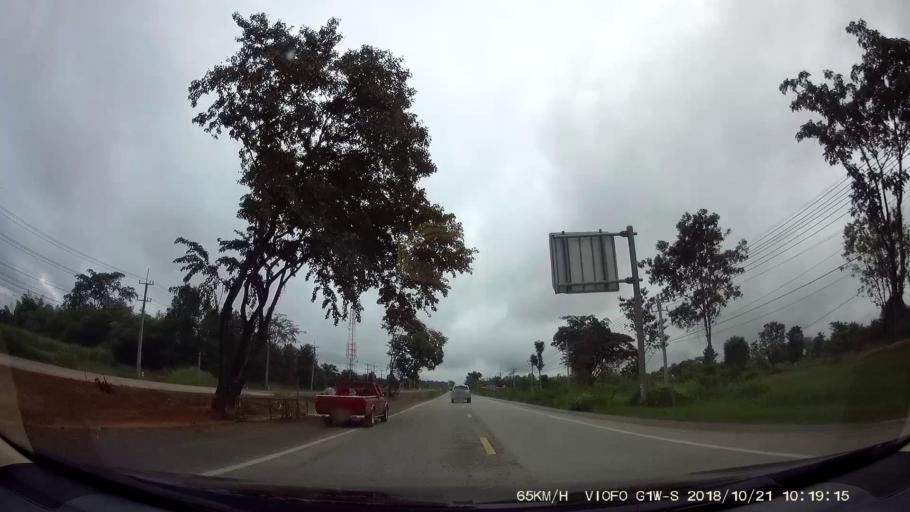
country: TH
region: Chaiyaphum
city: Phu Khiao
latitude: 16.3162
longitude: 102.1973
